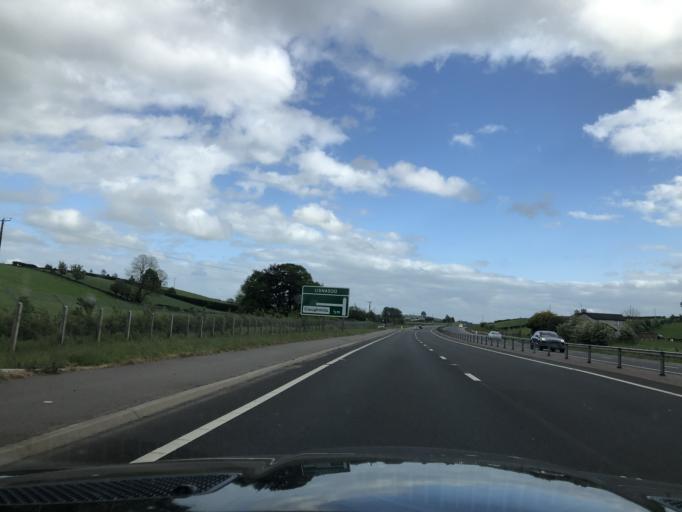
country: GB
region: Northern Ireland
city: Dunloy
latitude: 54.9934
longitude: -6.3509
